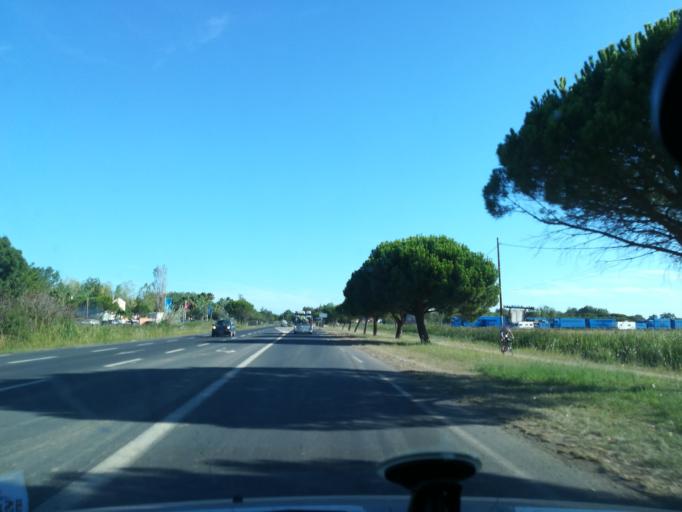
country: FR
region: Languedoc-Roussillon
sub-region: Departement de l'Herault
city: Portiragnes
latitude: 43.2865
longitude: 3.3626
